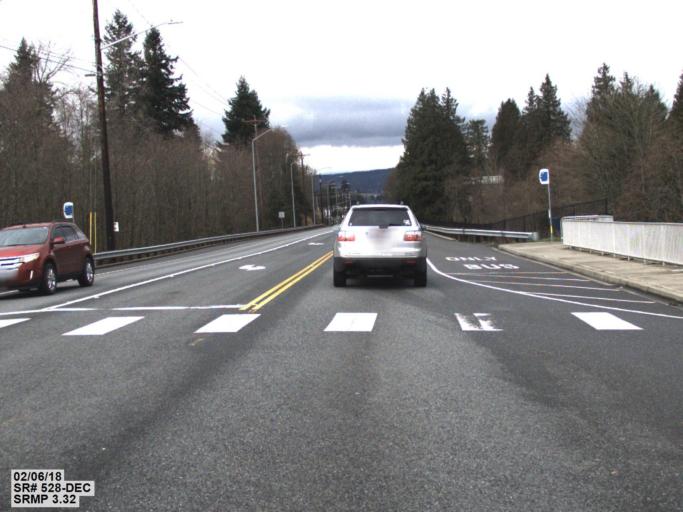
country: US
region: Washington
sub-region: Snohomish County
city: West Lake Stevens
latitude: 48.0535
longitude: -122.1139
